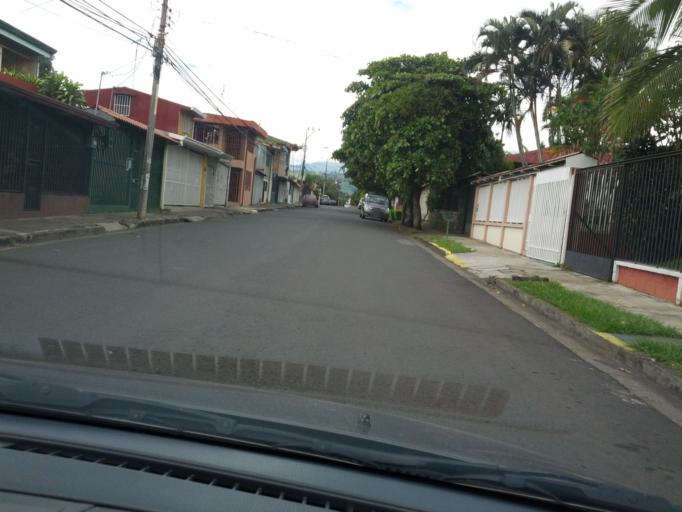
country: CR
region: Alajuela
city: Alajuela
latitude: 10.0214
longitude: -84.2130
